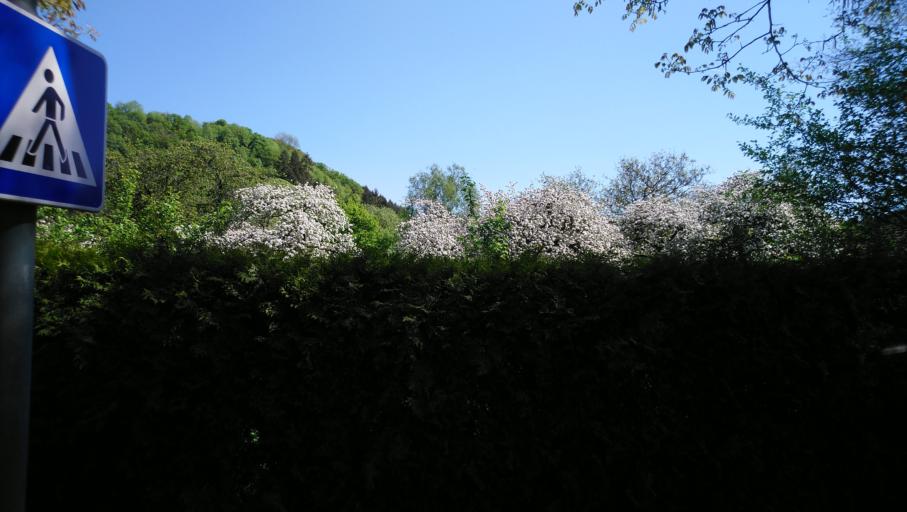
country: LU
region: Diekirch
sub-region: Canton de Vianden
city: Vianden
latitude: 49.9206
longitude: 6.2251
